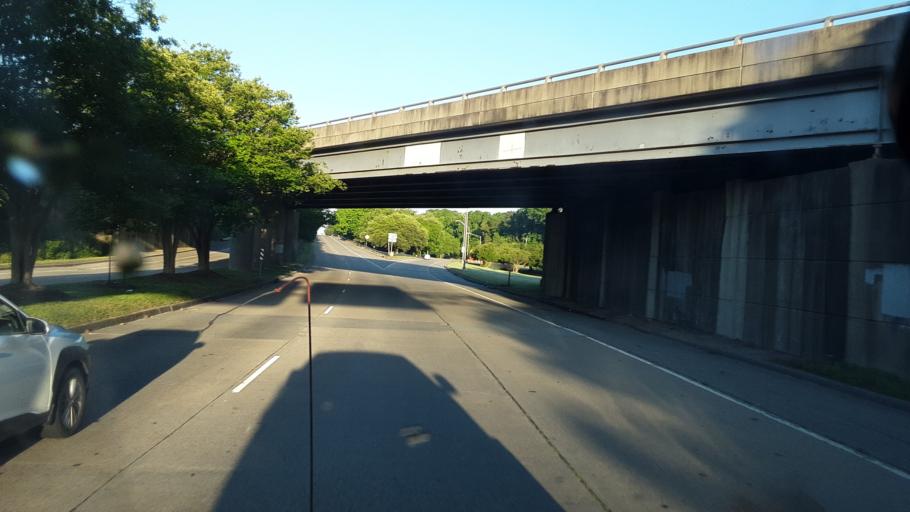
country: US
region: Virginia
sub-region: City of Virginia Beach
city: Virginia Beach
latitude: 36.8441
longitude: -76.0386
